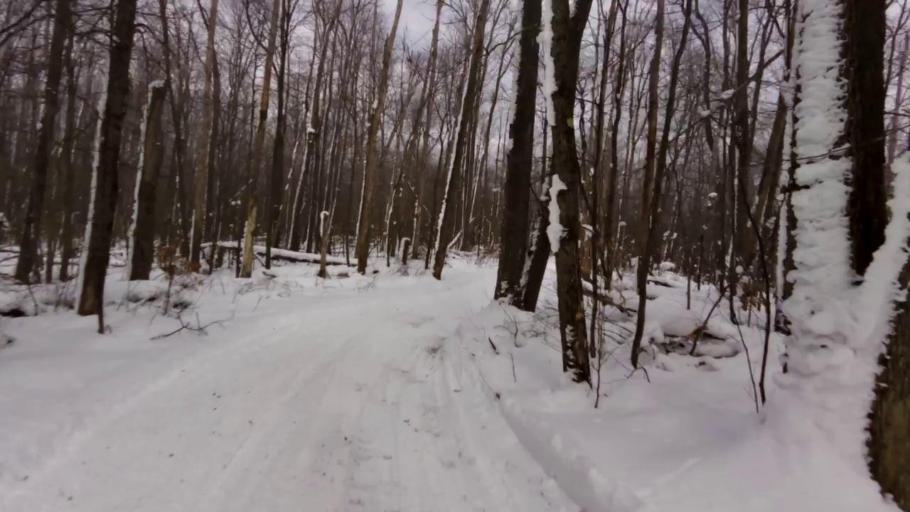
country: US
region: New York
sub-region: Cattaraugus County
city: Salamanca
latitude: 42.0383
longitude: -78.7530
